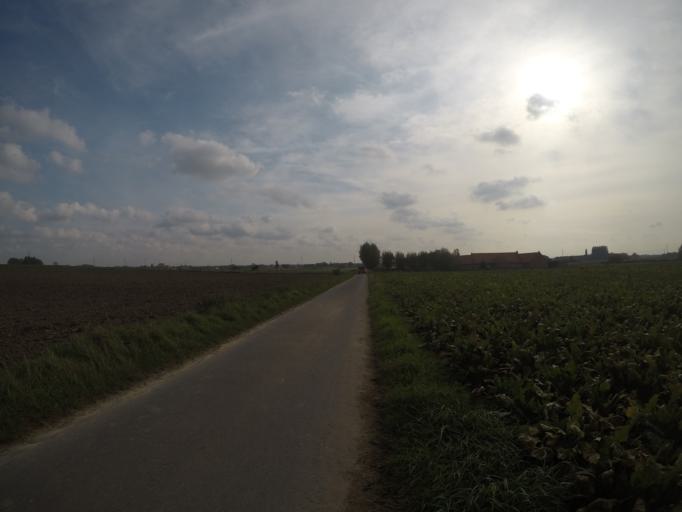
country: BE
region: Flanders
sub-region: Provincie West-Vlaanderen
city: Ledegem
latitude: 50.8391
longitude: 3.0737
